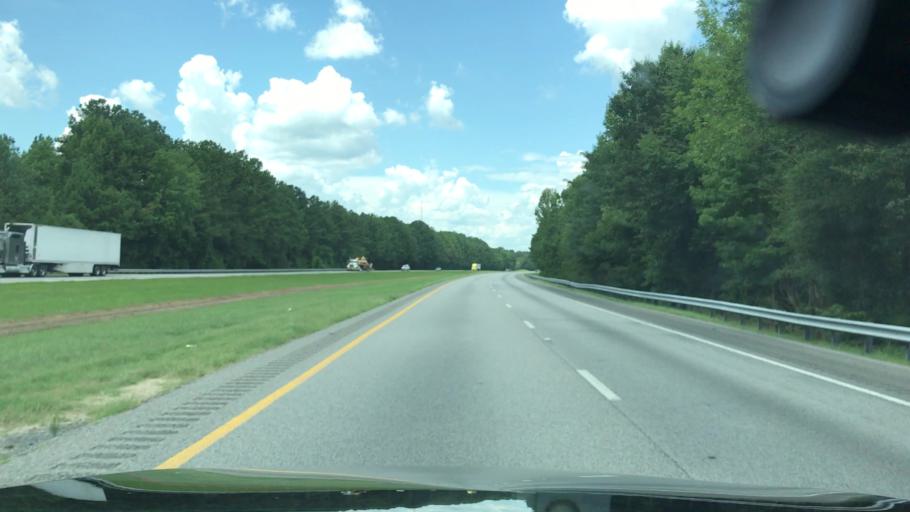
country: US
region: South Carolina
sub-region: Chester County
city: Great Falls
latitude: 34.5520
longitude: -81.0068
